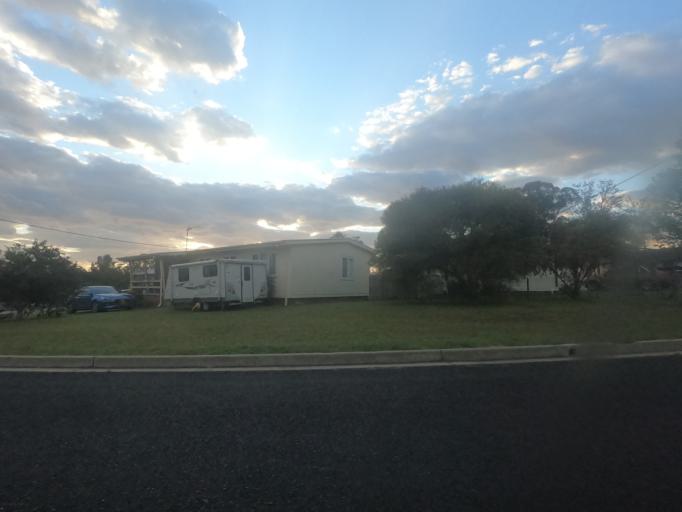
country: AU
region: New South Wales
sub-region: Wollongong
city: Koonawarra
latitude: -34.5012
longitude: 150.8102
